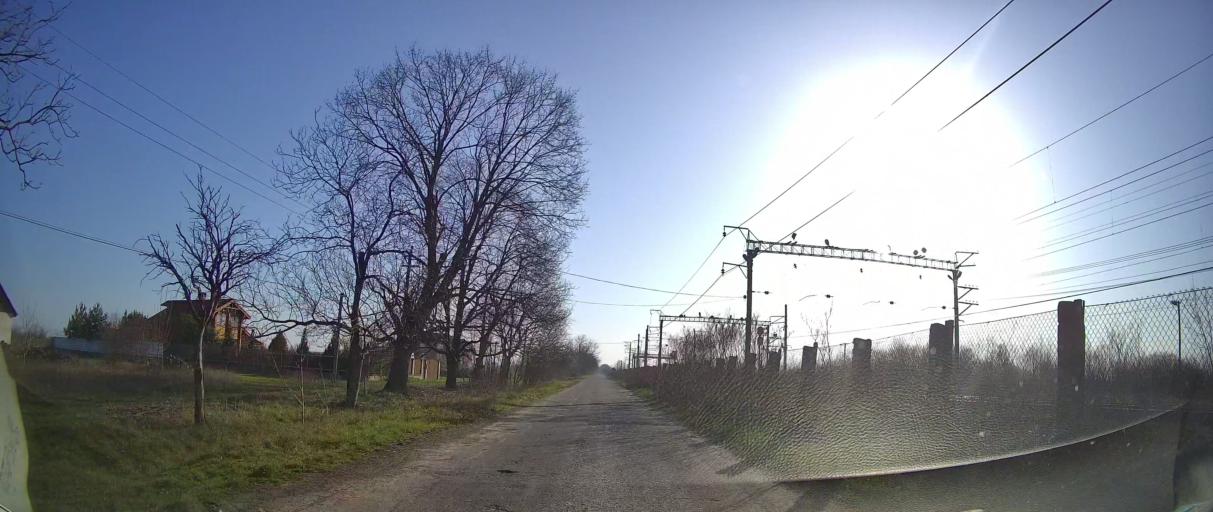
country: UA
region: Zakarpattia
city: Storozhnytsya
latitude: 48.5651
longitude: 22.1775
